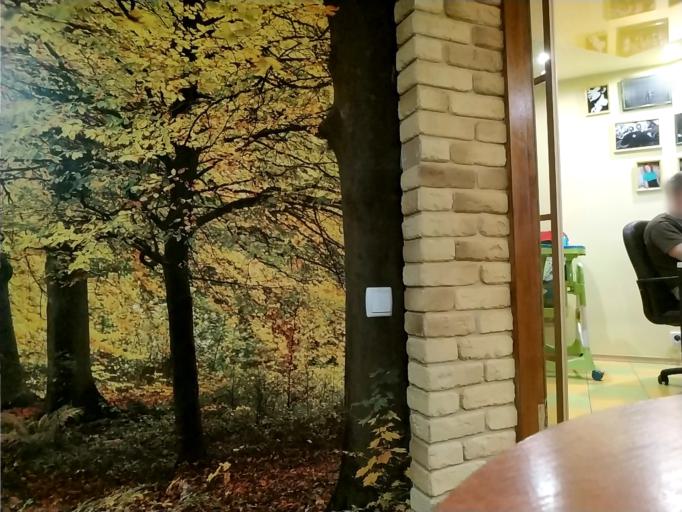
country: RU
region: Tverskaya
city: Zapadnaya Dvina
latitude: 56.3290
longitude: 31.8949
